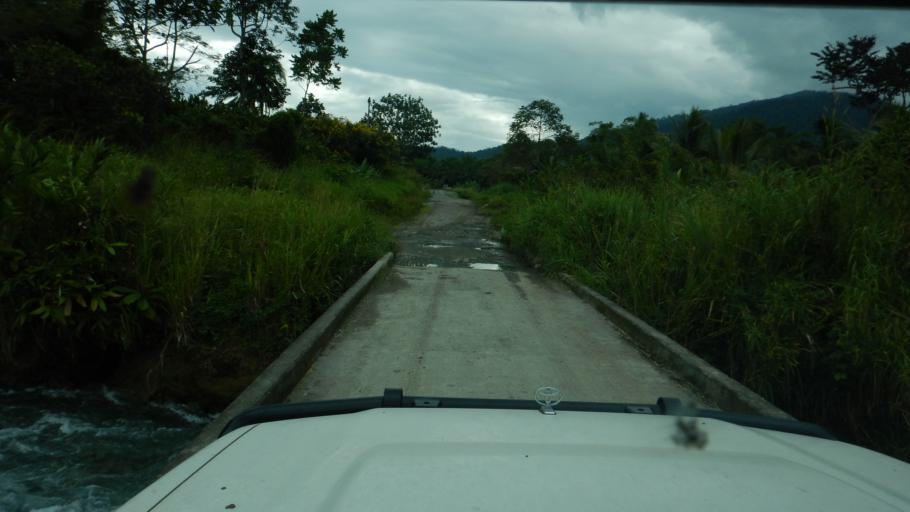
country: PG
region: Northern Province
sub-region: Sohe
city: Kokoda
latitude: -8.9183
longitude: 147.8719
